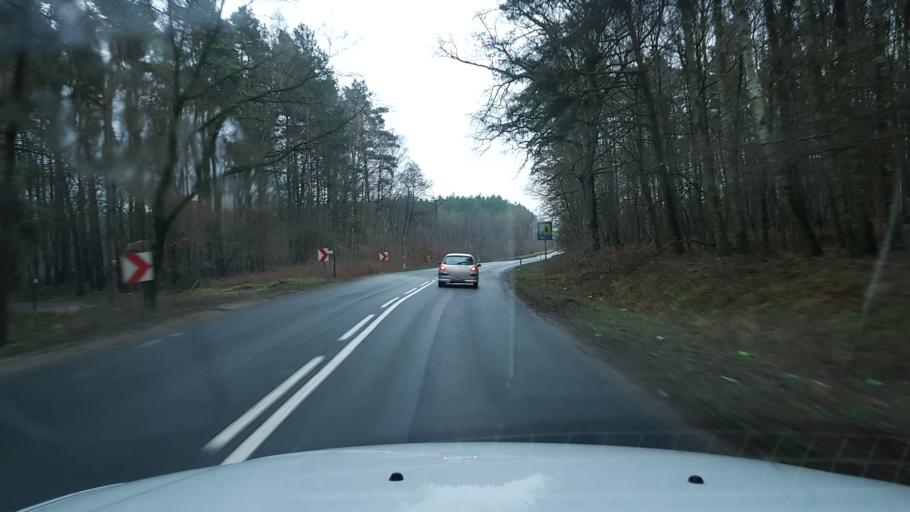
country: PL
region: West Pomeranian Voivodeship
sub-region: Powiat gryficki
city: Gryfice
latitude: 53.8593
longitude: 15.2254
